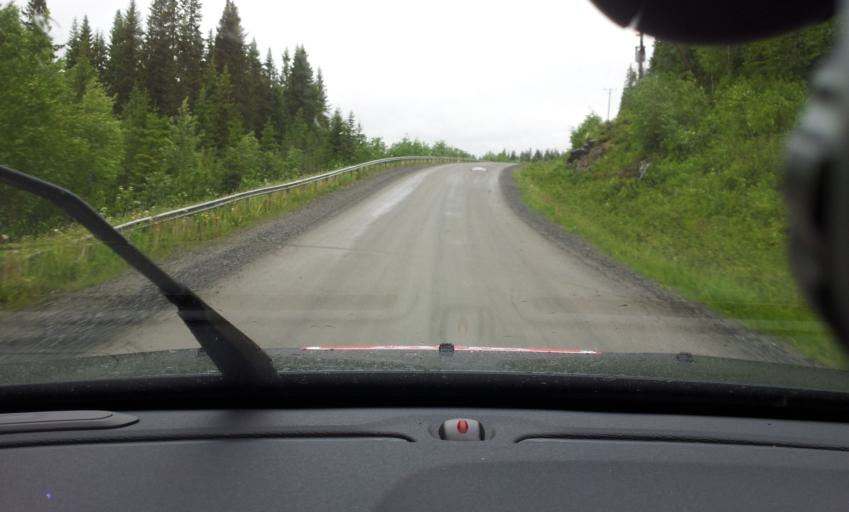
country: SE
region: Jaemtland
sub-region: Are Kommun
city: Are
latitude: 63.4028
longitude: 12.8382
